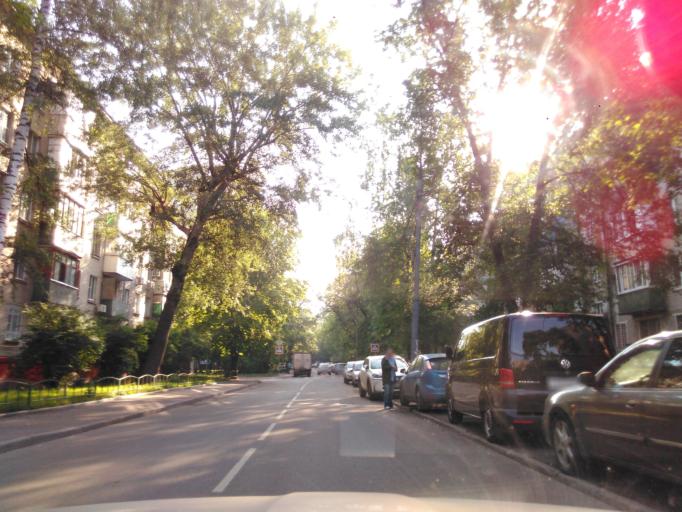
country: RU
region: Moskovskaya
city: Koptevo
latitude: 55.8165
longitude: 37.4936
